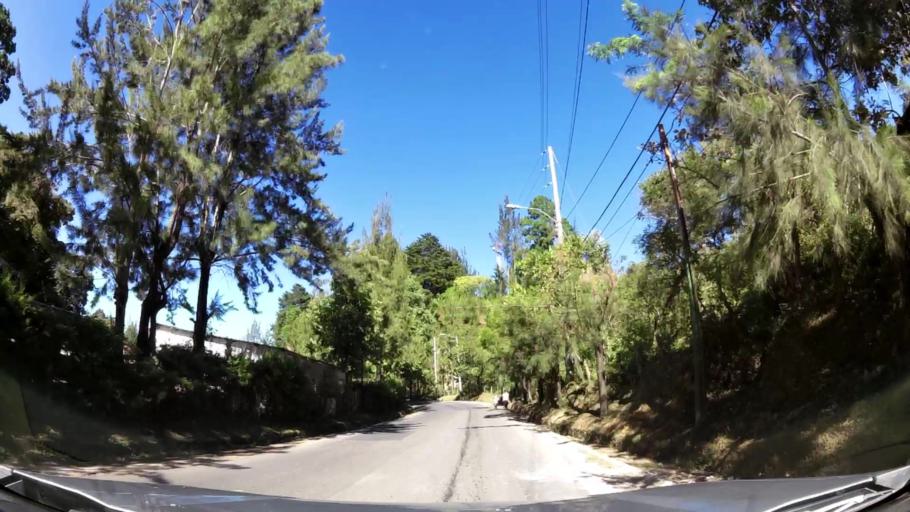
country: GT
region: Guatemala
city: Fraijanes
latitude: 14.4548
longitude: -90.4399
